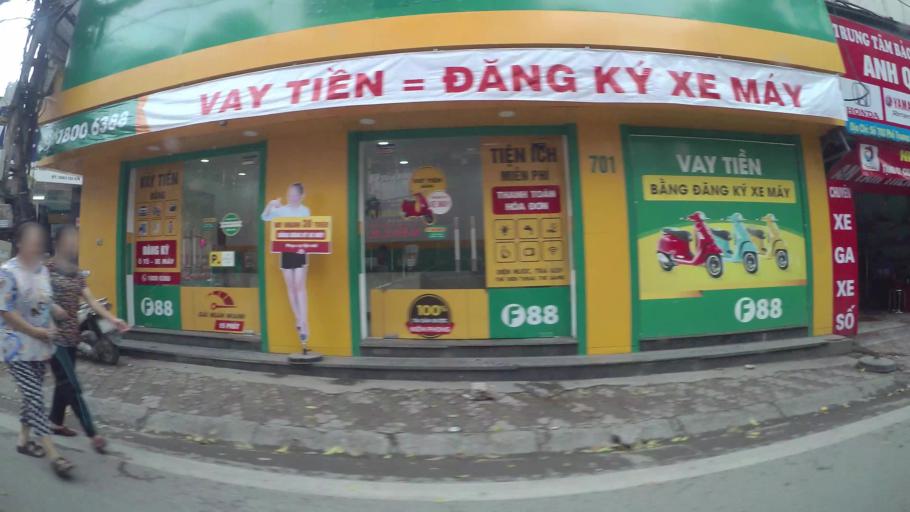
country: VN
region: Ha Noi
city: Van Dien
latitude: 20.9783
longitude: 105.8426
